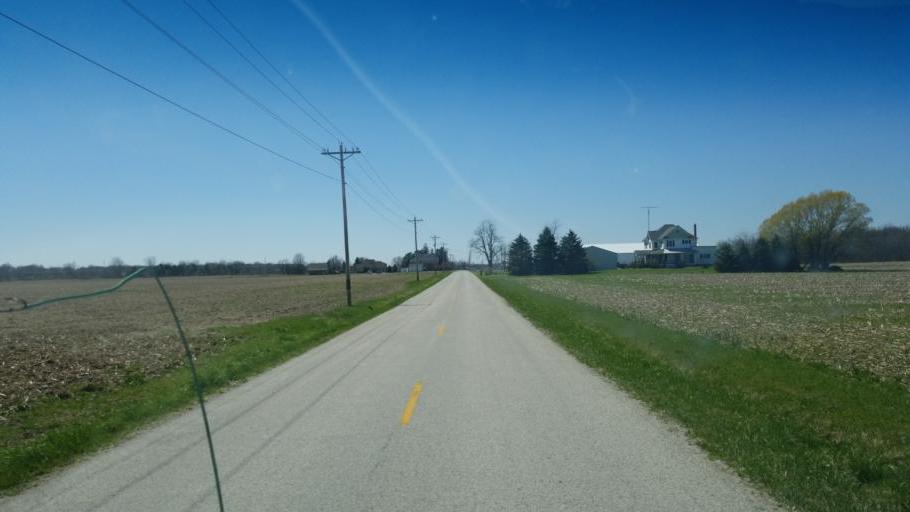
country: US
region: Ohio
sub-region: Crawford County
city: Bucyrus
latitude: 41.0229
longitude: -82.9490
